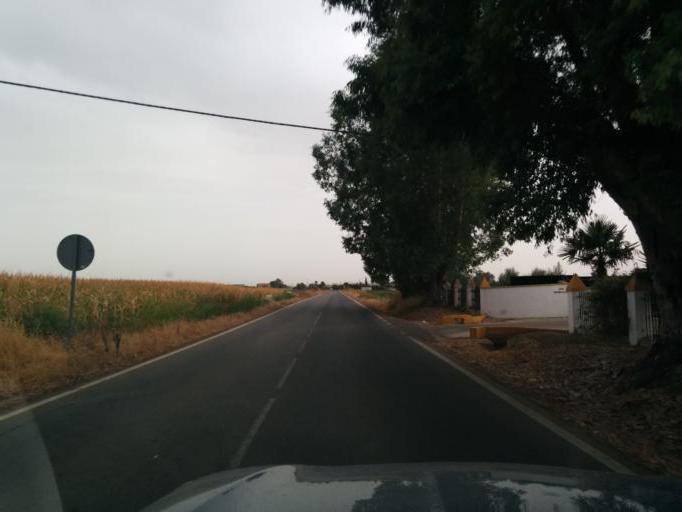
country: ES
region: Andalusia
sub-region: Provincia de Sevilla
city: Guillena
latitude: 37.5521
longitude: -6.0365
